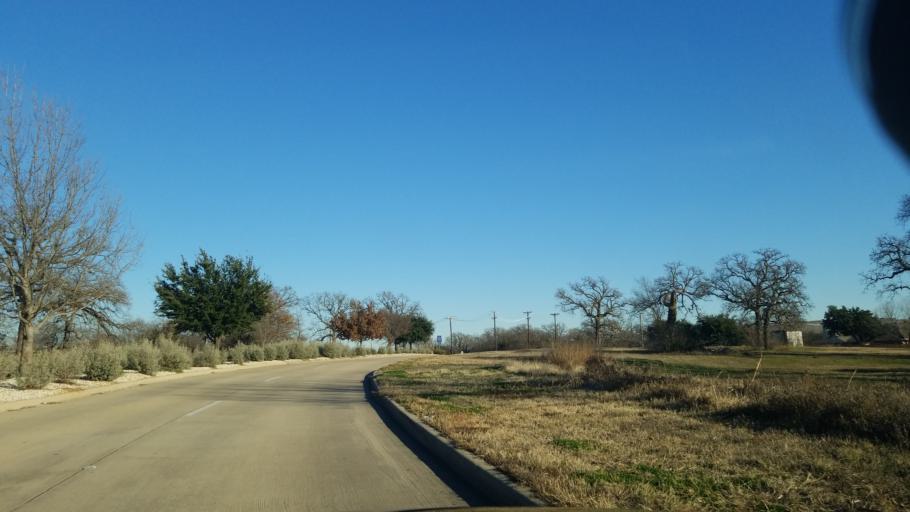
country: US
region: Texas
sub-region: Denton County
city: Hickory Creek
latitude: 33.1269
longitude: -97.0407
